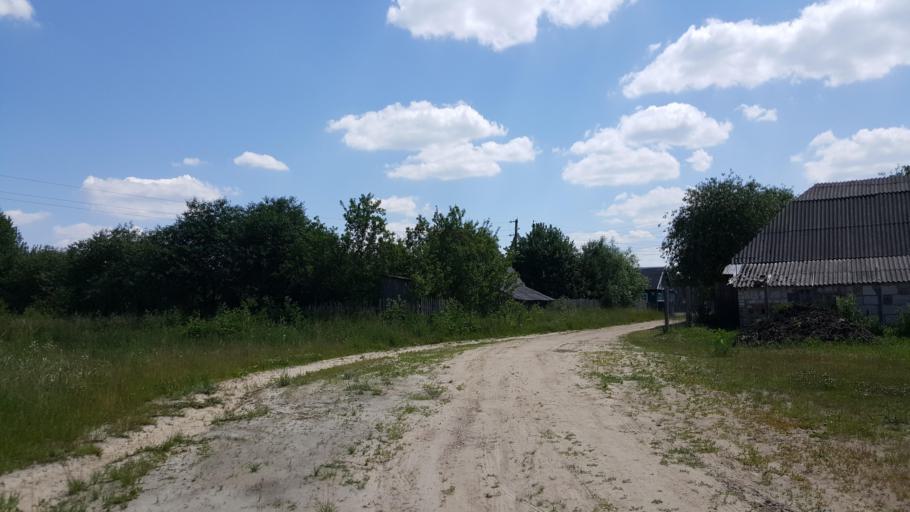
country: BY
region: Brest
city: Kamyanyets
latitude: 52.4095
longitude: 23.8295
